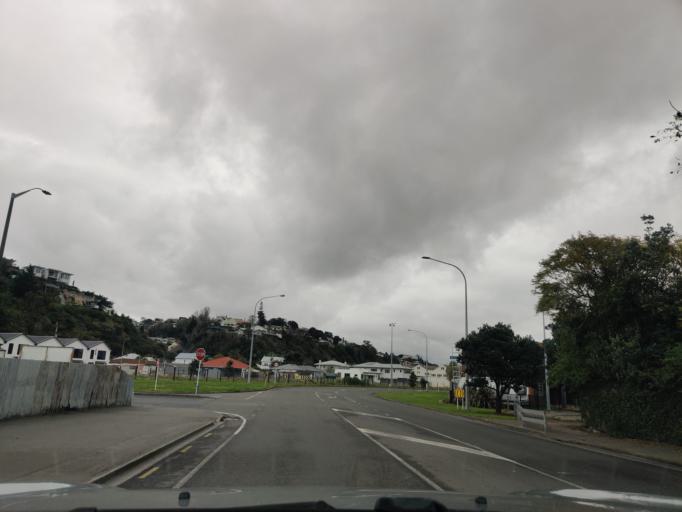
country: NZ
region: Hawke's Bay
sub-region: Napier City
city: Napier
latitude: -39.4786
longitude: 176.9078
